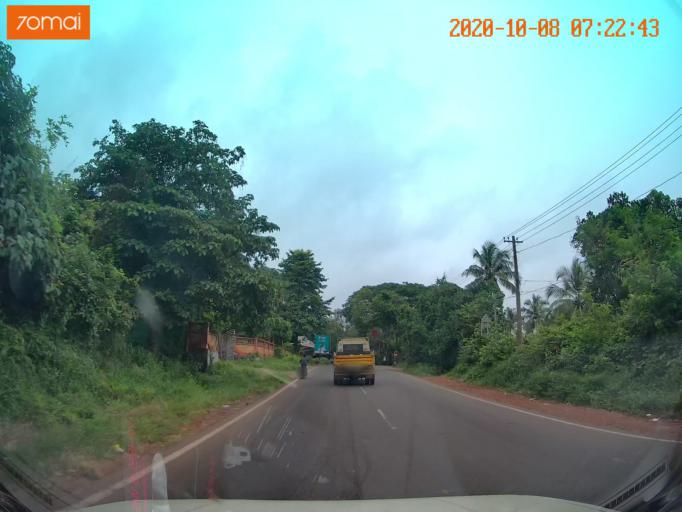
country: IN
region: Kerala
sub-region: Malappuram
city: Tirur
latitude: 10.8671
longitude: 76.0416
